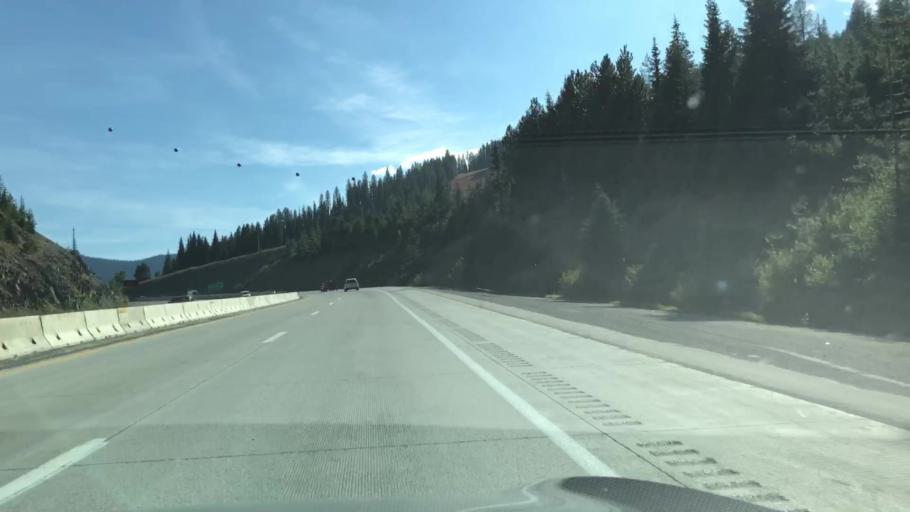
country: US
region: Idaho
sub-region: Shoshone County
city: Wallace
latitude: 47.4591
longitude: -115.6945
